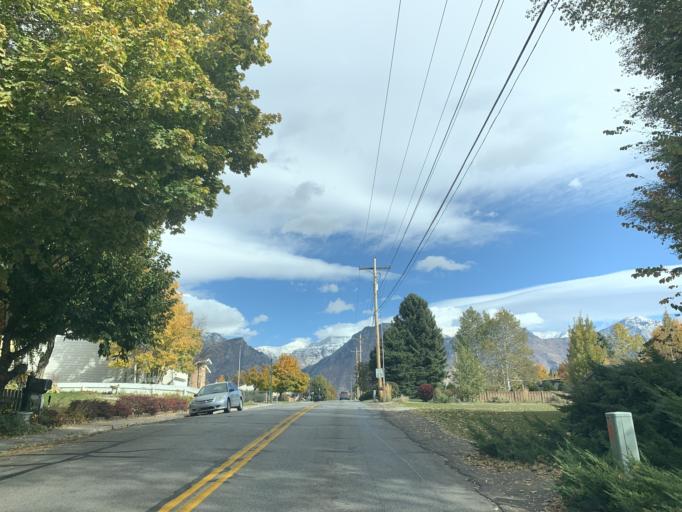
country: US
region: Utah
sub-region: Utah County
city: Orem
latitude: 40.2606
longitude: -111.6930
